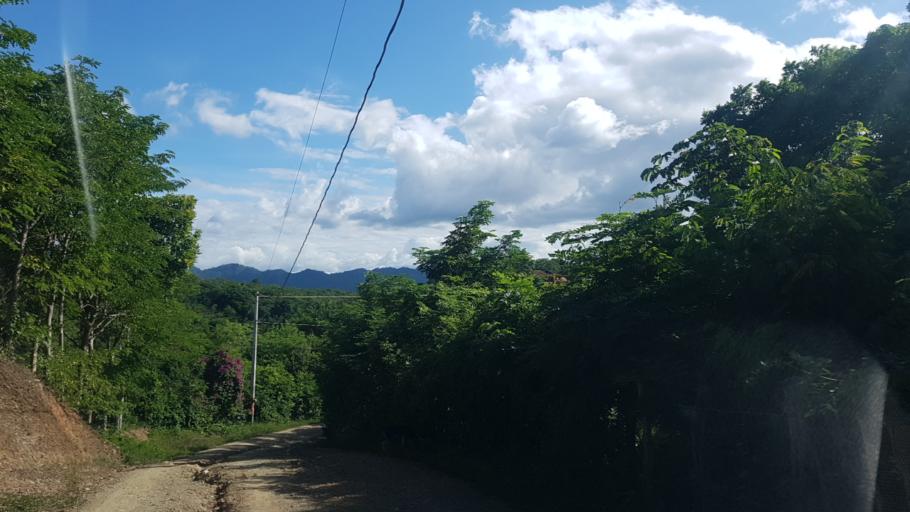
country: NI
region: Nueva Segovia
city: Mozonte
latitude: 13.6435
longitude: -86.3974
